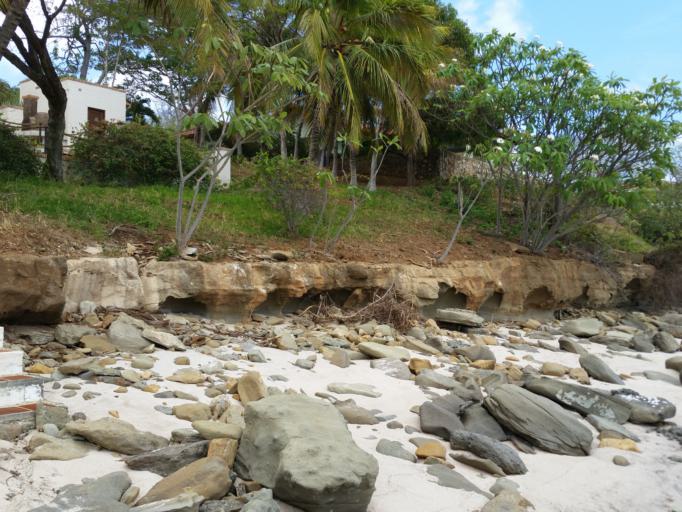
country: NI
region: Rivas
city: Tola
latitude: 11.4350
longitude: -86.0839
